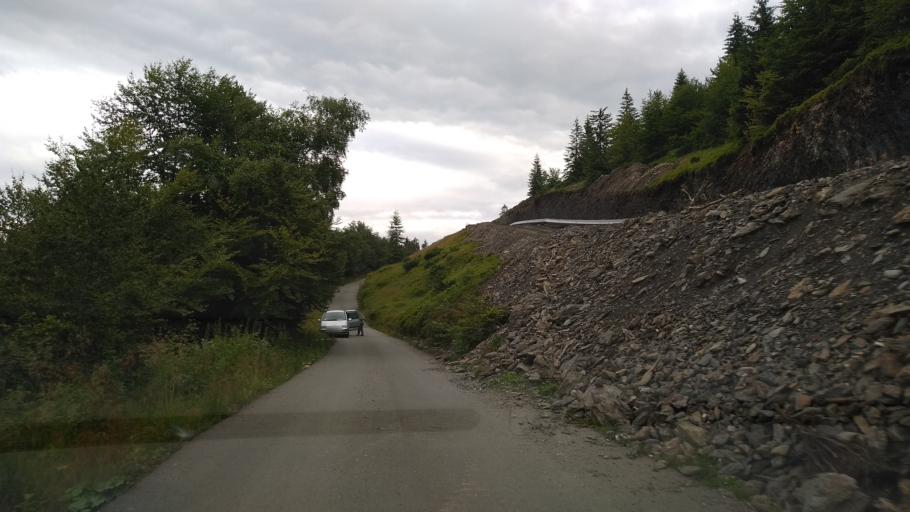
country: RO
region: Hunedoara
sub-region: Municipiul  Vulcan
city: Jiu-Paroseni
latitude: 45.3195
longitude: 23.3006
